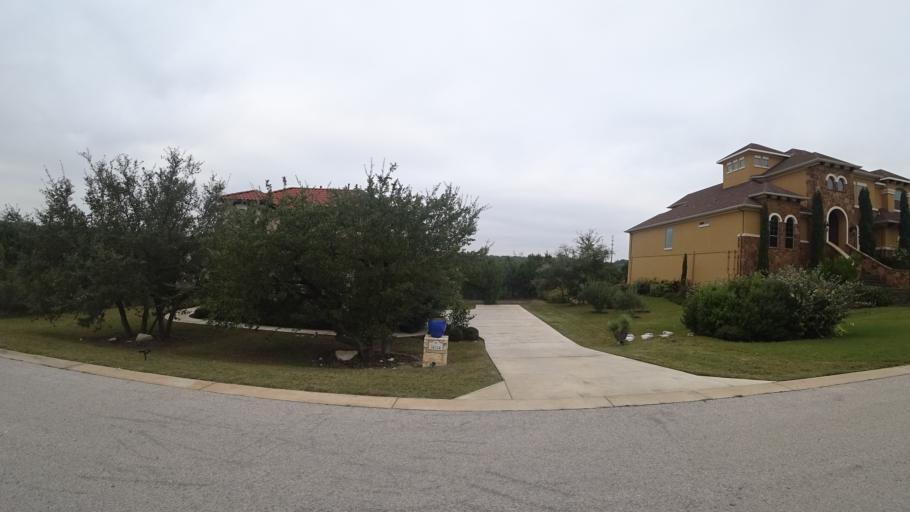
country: US
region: Texas
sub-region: Travis County
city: Hudson Bend
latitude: 30.3913
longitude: -97.9215
